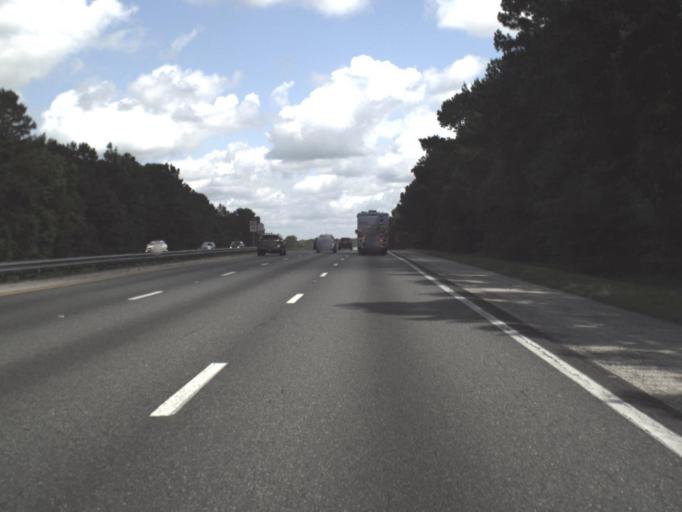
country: US
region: Florida
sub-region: Alachua County
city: Alachua
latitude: 29.7656
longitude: -82.5047
